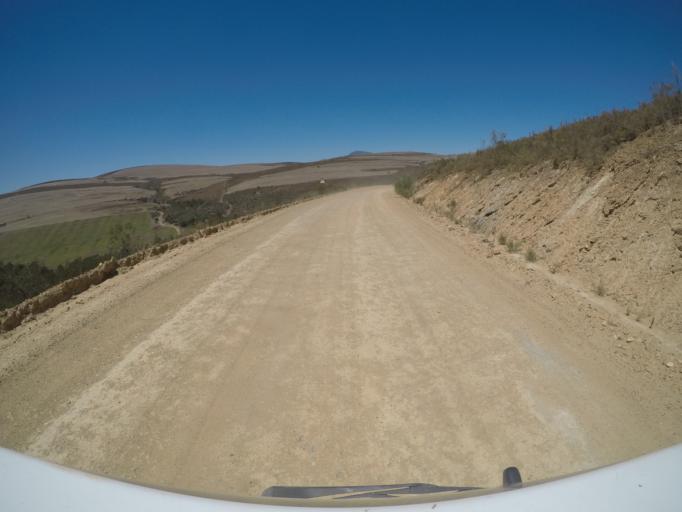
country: ZA
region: Western Cape
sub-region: Overberg District Municipality
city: Grabouw
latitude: -34.2050
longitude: 19.2159
